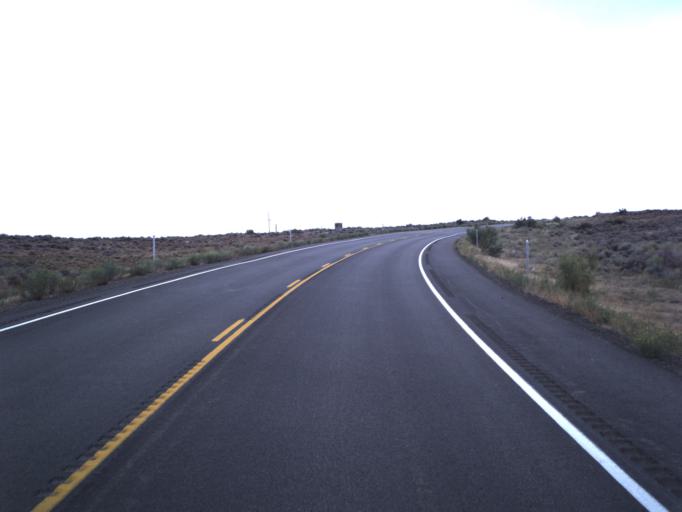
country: US
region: Utah
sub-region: Uintah County
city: Naples
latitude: 40.2083
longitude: -109.3631
